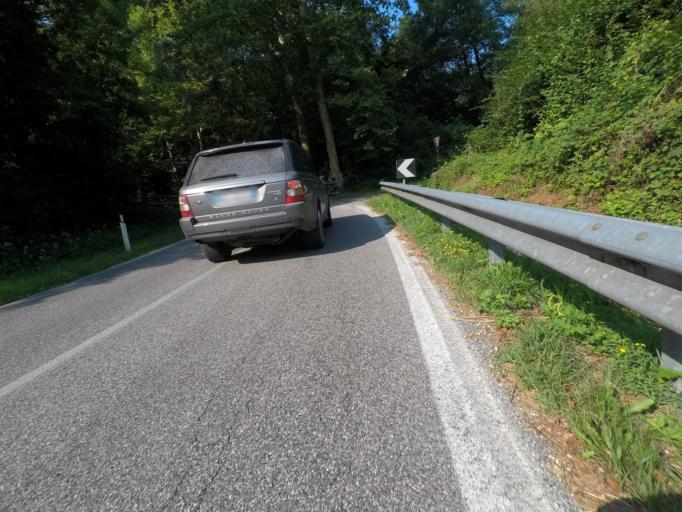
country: IT
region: Friuli Venezia Giulia
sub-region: Provincia di Pordenone
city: Pinzano al Tagliamento
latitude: 46.1872
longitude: 12.9468
